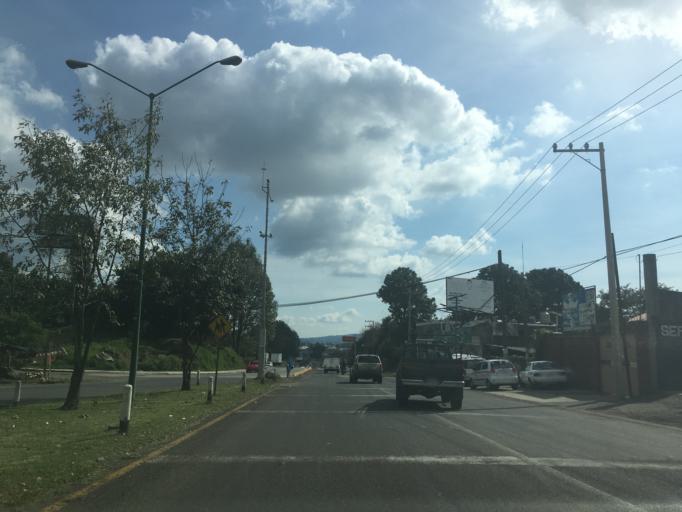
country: MX
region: Michoacan
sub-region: Uruapan
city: Toreo Bajo (El Toreo Bajo)
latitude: 19.4302
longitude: -102.0251
